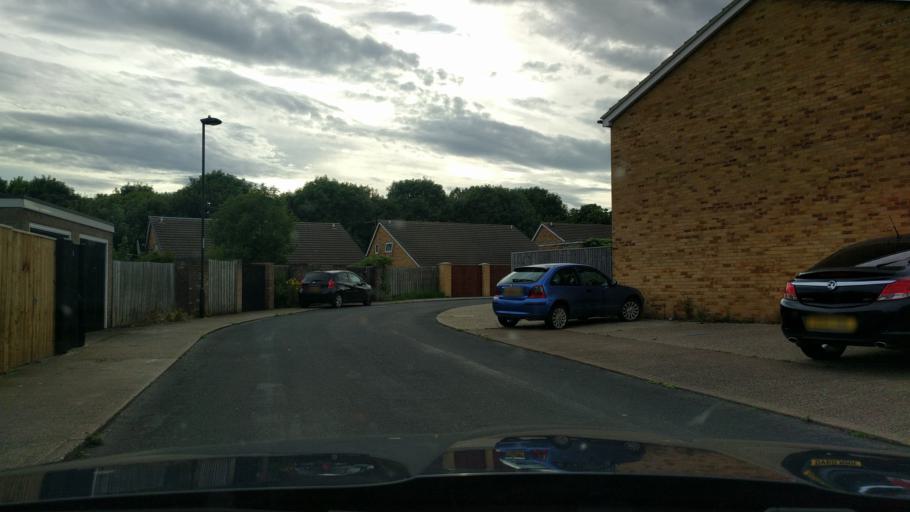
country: GB
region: England
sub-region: Borough of North Tyneside
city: Shiremoor
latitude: 55.0206
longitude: -1.4881
